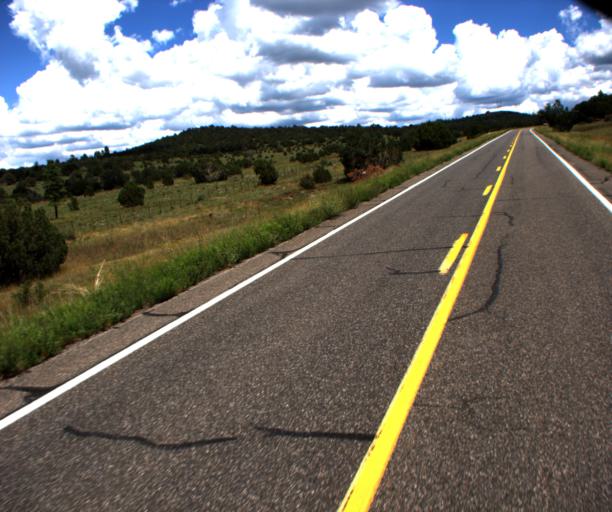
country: US
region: Arizona
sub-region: Gila County
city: Pine
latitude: 34.5081
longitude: -111.5618
